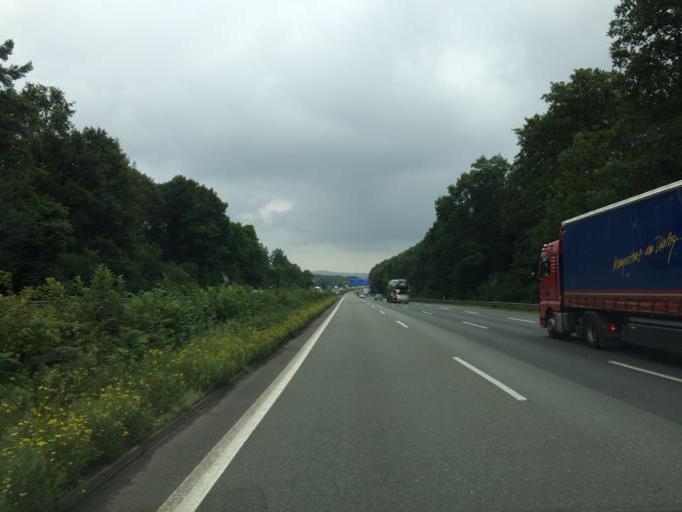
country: DE
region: North Rhine-Westphalia
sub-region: Regierungsbezirk Detmold
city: Verl
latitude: 51.9314
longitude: 8.5326
